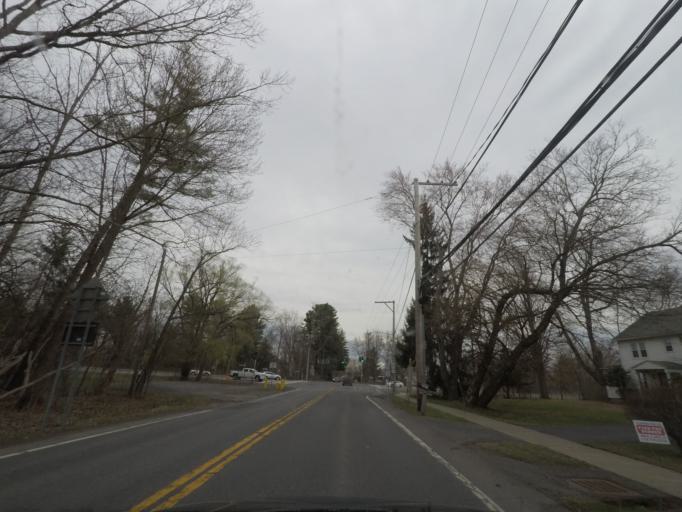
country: US
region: New York
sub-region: Albany County
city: Delmar
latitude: 42.6087
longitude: -73.8196
